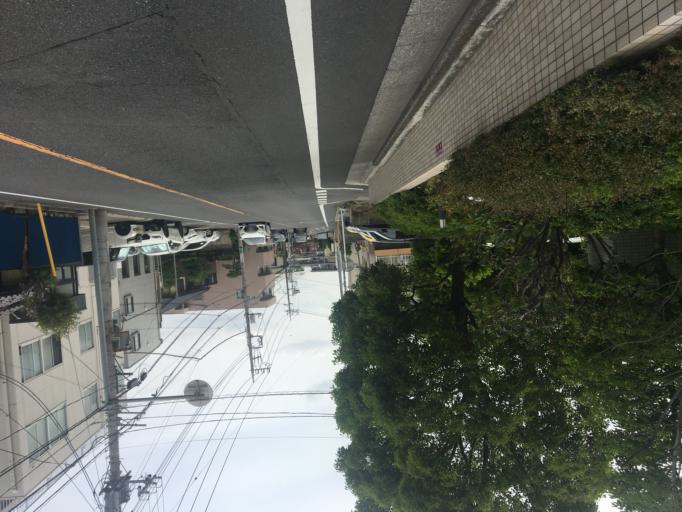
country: JP
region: Saitama
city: Shimotoda
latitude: 35.8420
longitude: 139.6597
